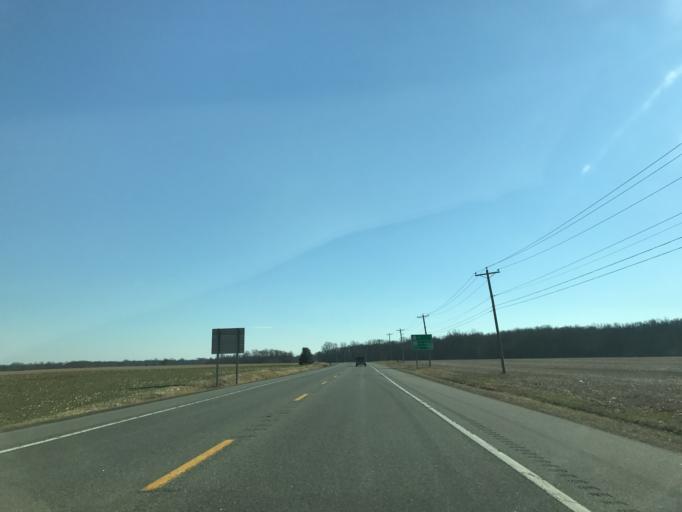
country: US
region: Maryland
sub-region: Queen Anne's County
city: Centreville
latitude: 39.0087
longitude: -76.0753
